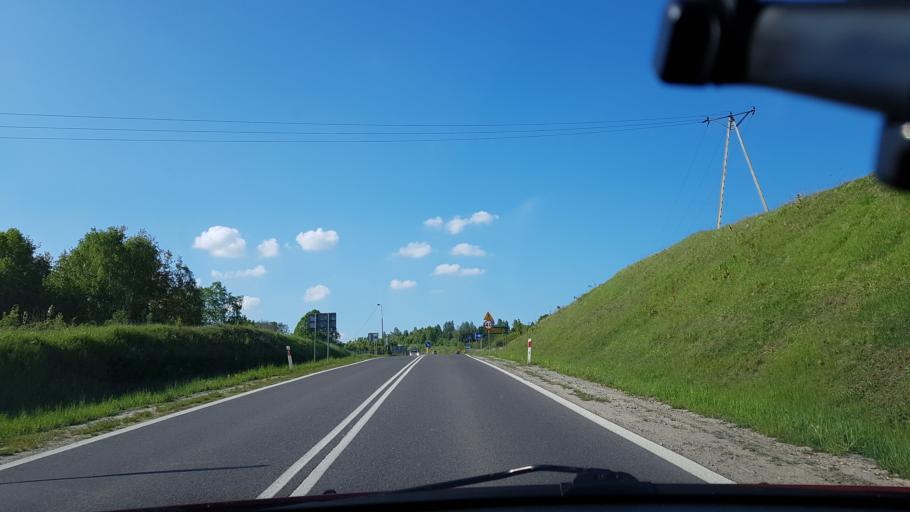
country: PL
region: Lower Silesian Voivodeship
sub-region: Powiat klodzki
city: Nowa Ruda
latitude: 50.5806
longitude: 16.5264
